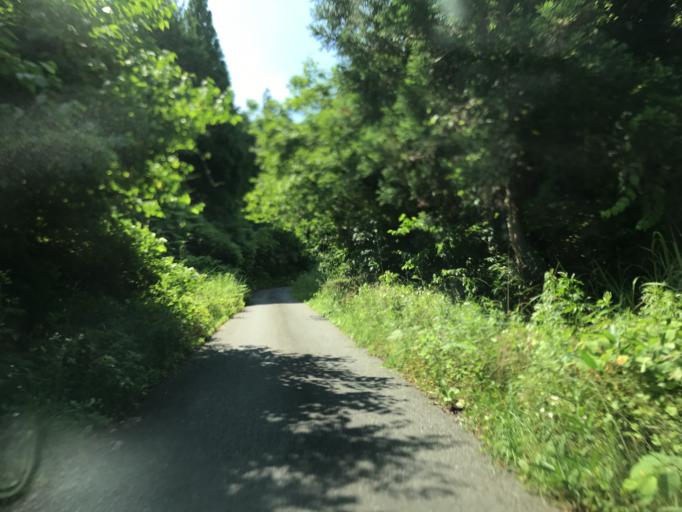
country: JP
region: Fukushima
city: Yanagawamachi-saiwaicho
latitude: 37.7730
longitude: 140.6542
